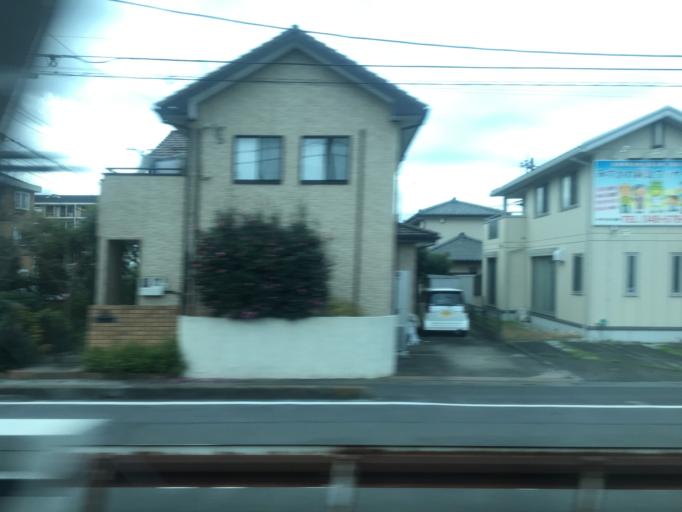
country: JP
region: Saitama
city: Okegawa
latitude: 35.9814
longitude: 139.5812
